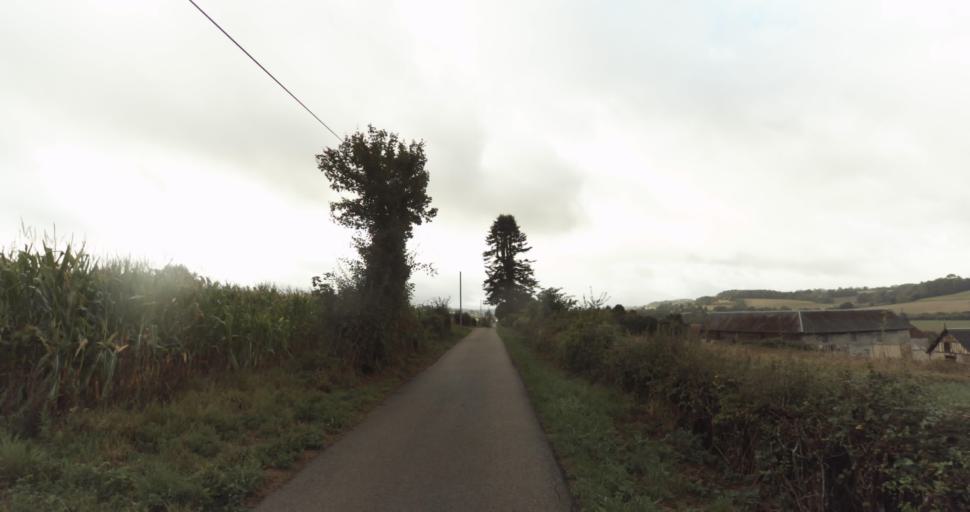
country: FR
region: Lower Normandy
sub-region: Departement de l'Orne
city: Vimoutiers
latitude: 48.8931
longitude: 0.2797
